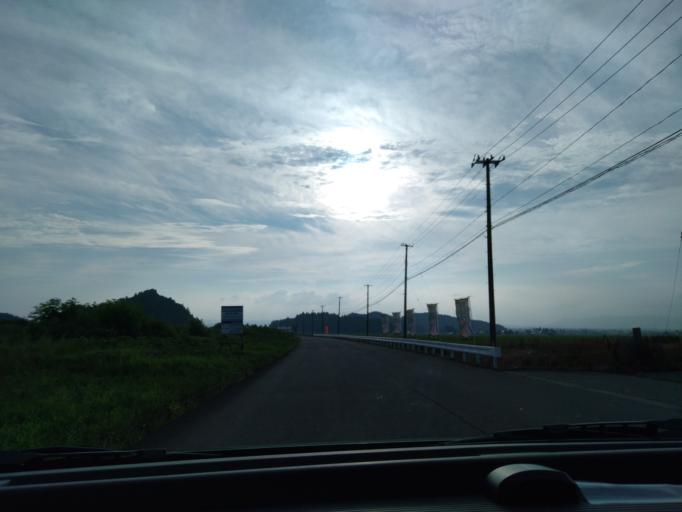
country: JP
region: Akita
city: Yokotemachi
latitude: 39.3776
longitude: 140.5650
